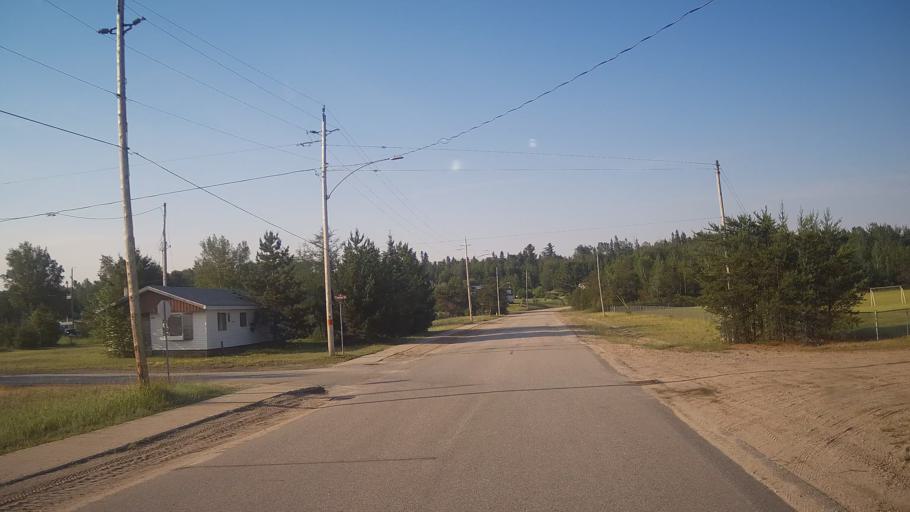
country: CA
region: Ontario
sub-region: Rainy River District
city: Atikokan
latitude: 49.4050
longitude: -91.6563
